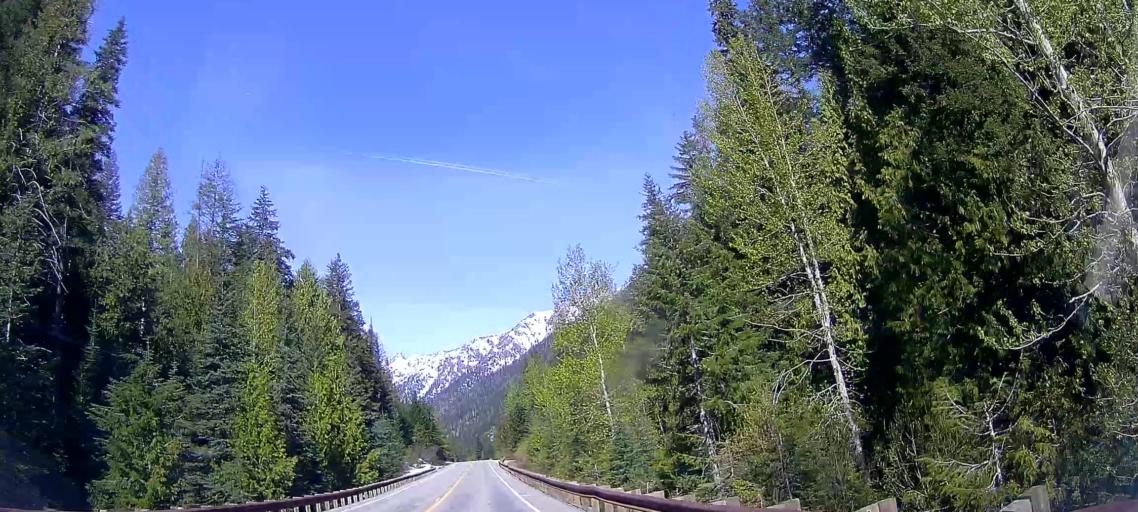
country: US
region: Washington
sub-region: Chelan County
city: Granite Falls
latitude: 48.6000
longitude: -120.5488
